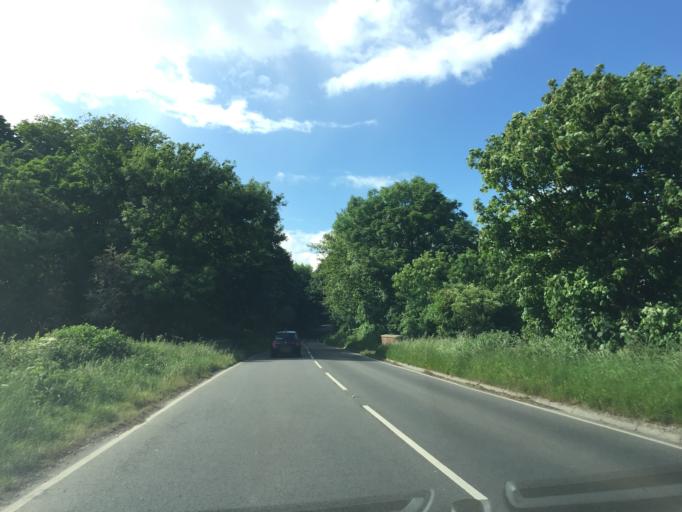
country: GB
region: England
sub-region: Dorset
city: Dorchester
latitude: 50.6988
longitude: -2.4104
